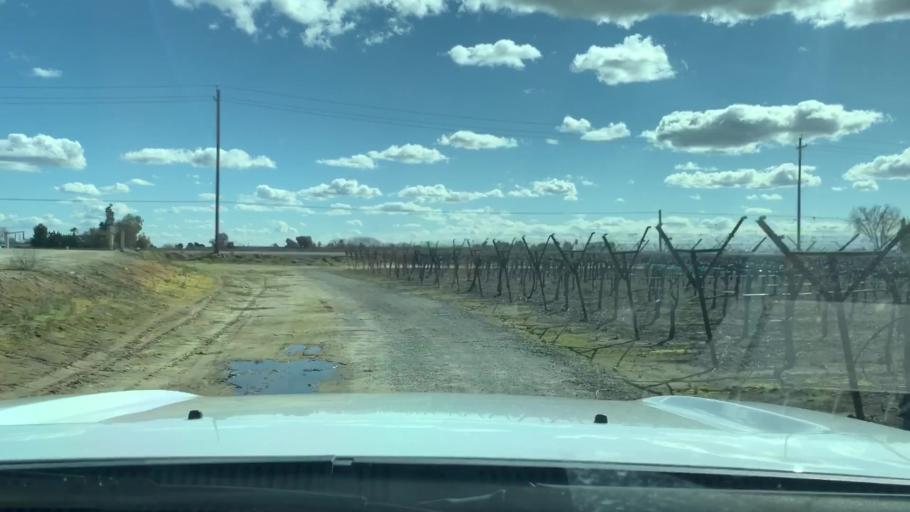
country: US
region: California
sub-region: Fresno County
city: Parlier
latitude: 36.6059
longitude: -119.5631
